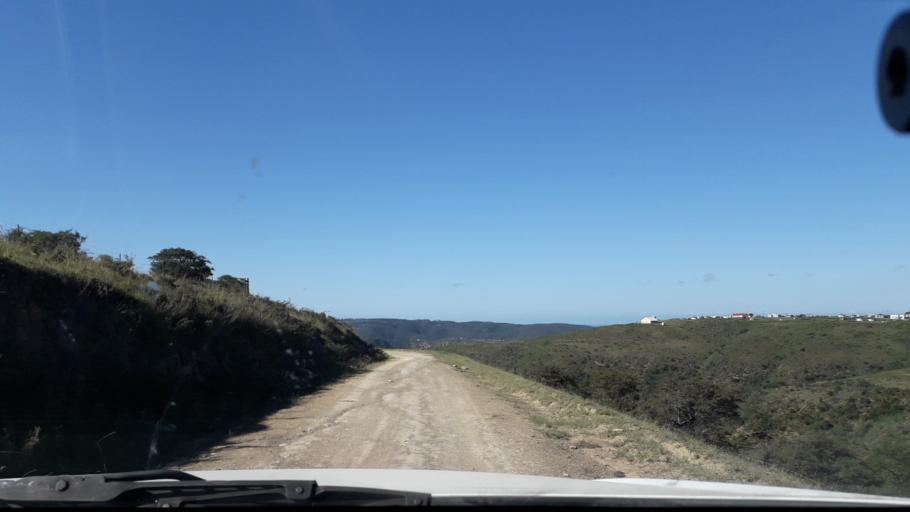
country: ZA
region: Eastern Cape
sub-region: Amathole District Municipality
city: Komga
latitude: -32.7860
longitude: 27.9541
